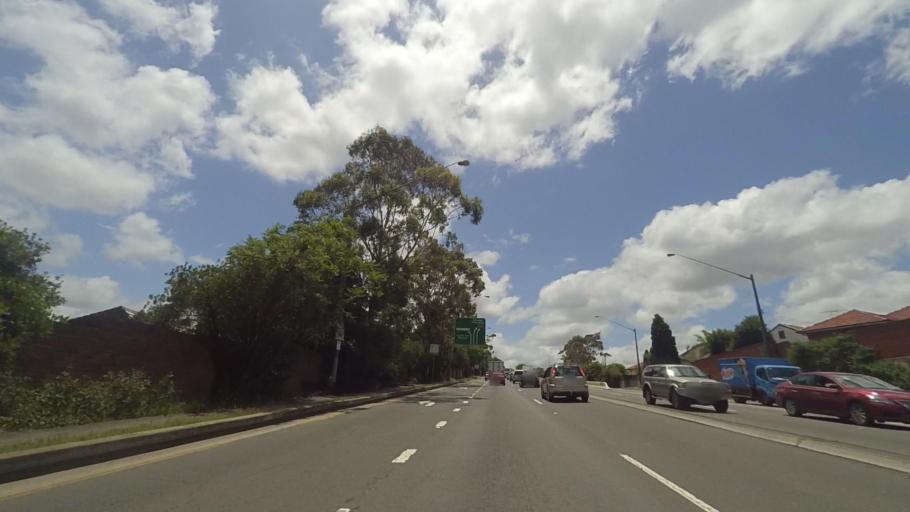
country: AU
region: New South Wales
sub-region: The Hills Shire
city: West Pennant
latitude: -33.7508
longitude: 151.0490
